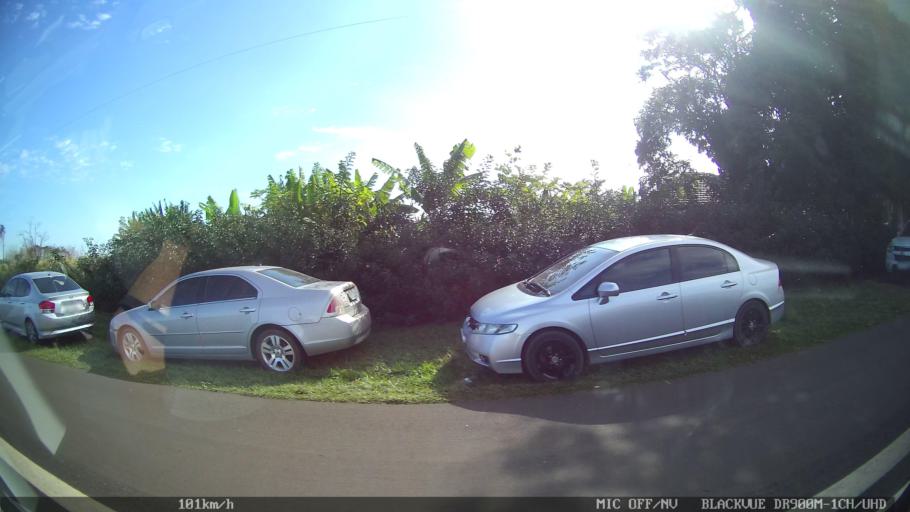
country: BR
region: Sao Paulo
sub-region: Iracemapolis
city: Iracemapolis
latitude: -22.6429
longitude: -47.5105
